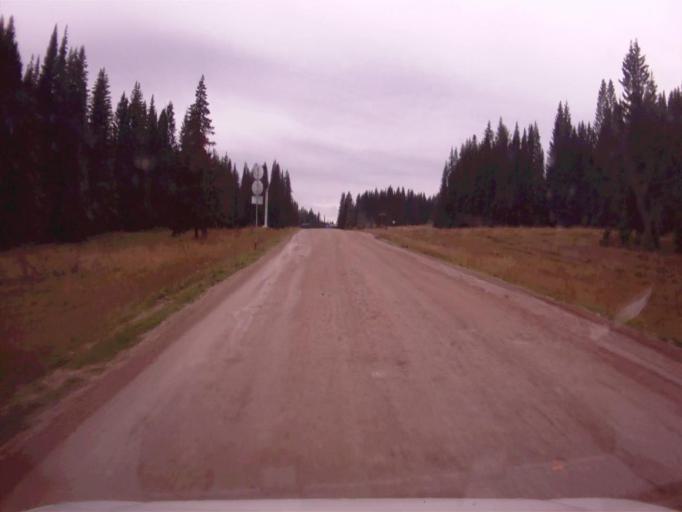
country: RU
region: Chelyabinsk
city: Nyazepetrovsk
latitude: 56.0594
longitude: 59.5602
